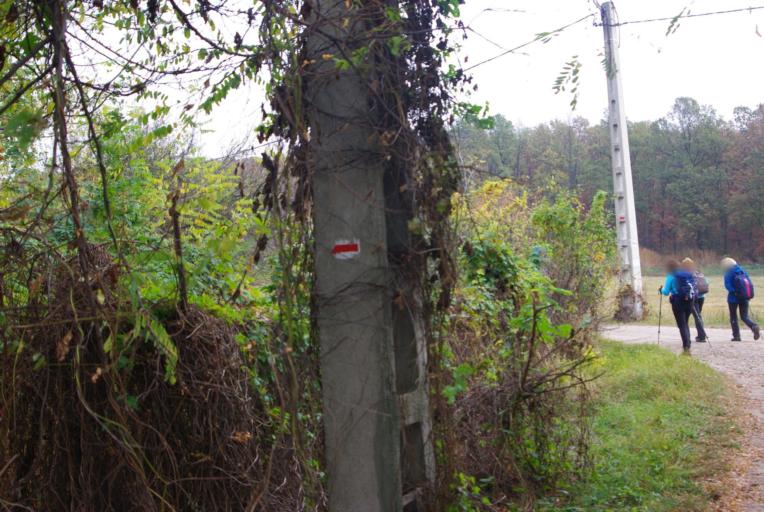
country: HU
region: Pest
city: Isaszeg
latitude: 47.5131
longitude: 19.3873
